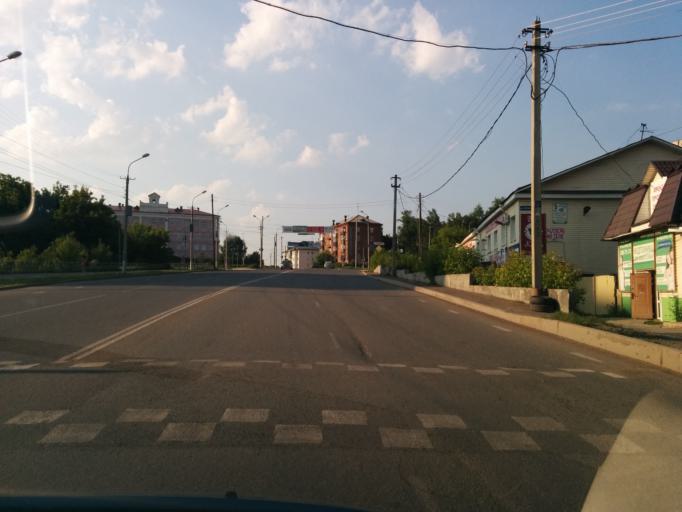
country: RU
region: Perm
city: Perm
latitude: 58.0014
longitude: 56.2077
